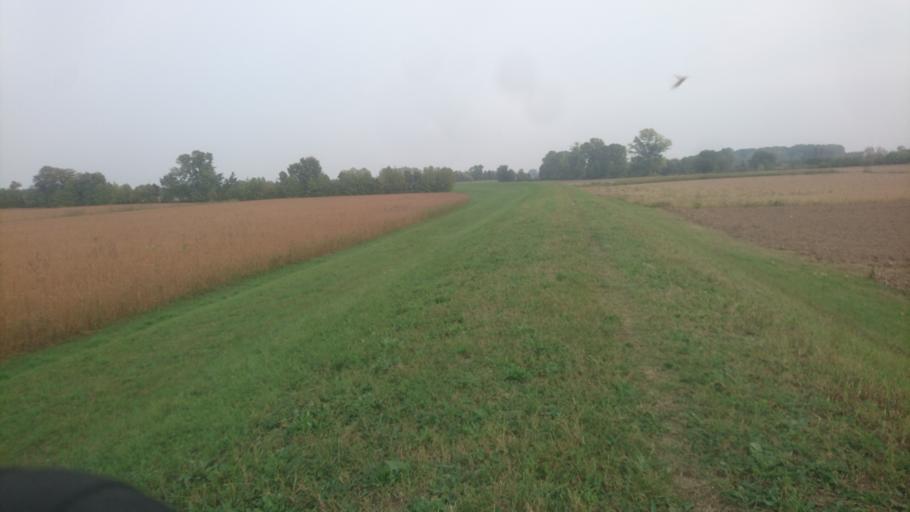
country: IT
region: Veneto
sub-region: Provincia di Padova
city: Cervarese Santa Croce
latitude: 45.4245
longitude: 11.7012
